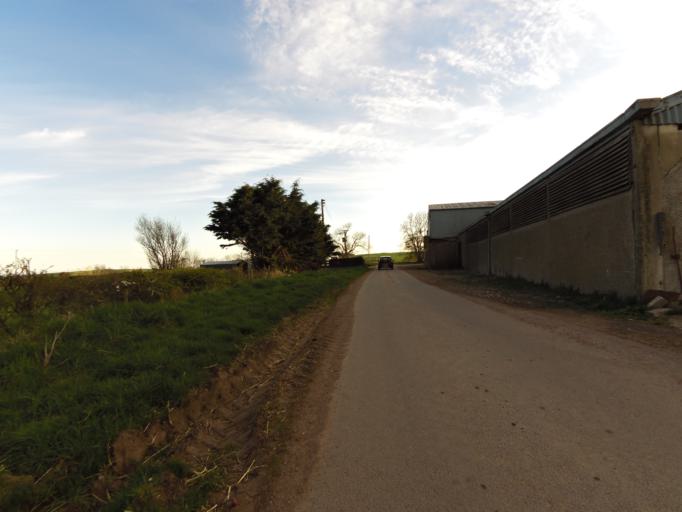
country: GB
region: Scotland
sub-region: Aberdeenshire
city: Inverbervie
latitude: 56.8924
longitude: -2.2337
